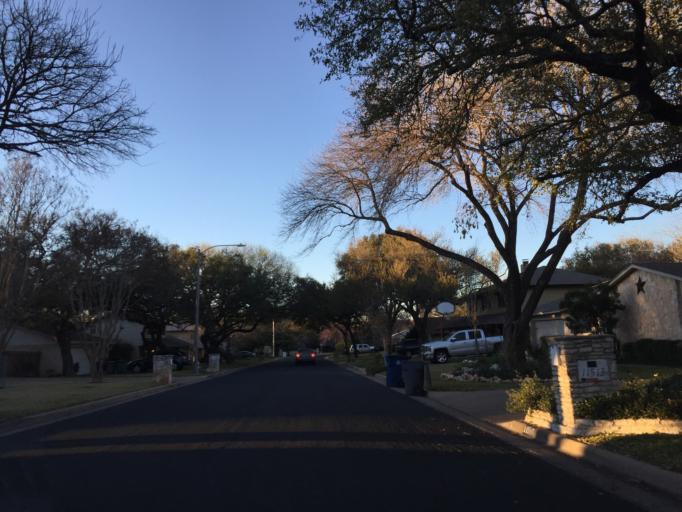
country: US
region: Texas
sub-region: Williamson County
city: Jollyville
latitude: 30.4302
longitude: -97.7766
